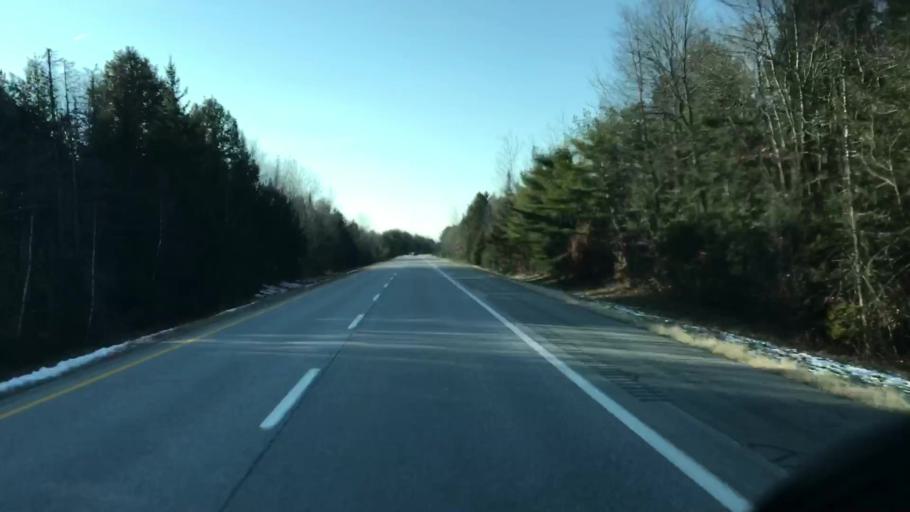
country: US
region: Maine
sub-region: Penobscot County
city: Carmel
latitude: 44.7742
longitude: -69.0225
